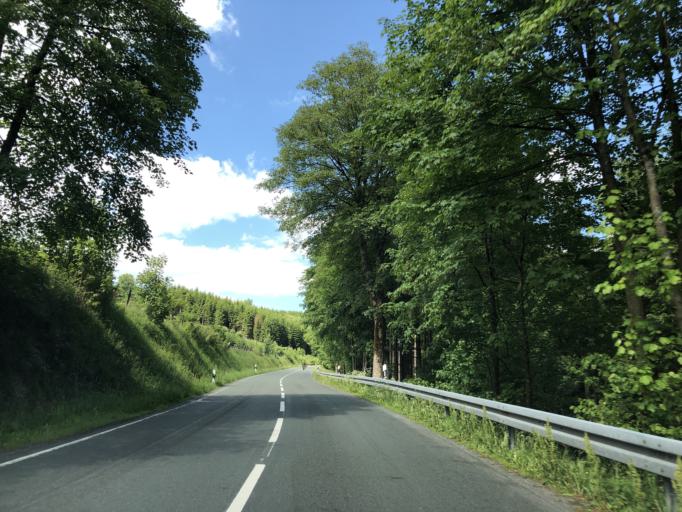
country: DE
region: North Rhine-Westphalia
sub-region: Regierungsbezirk Arnsberg
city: Winterberg
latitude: 51.1932
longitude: 8.4601
